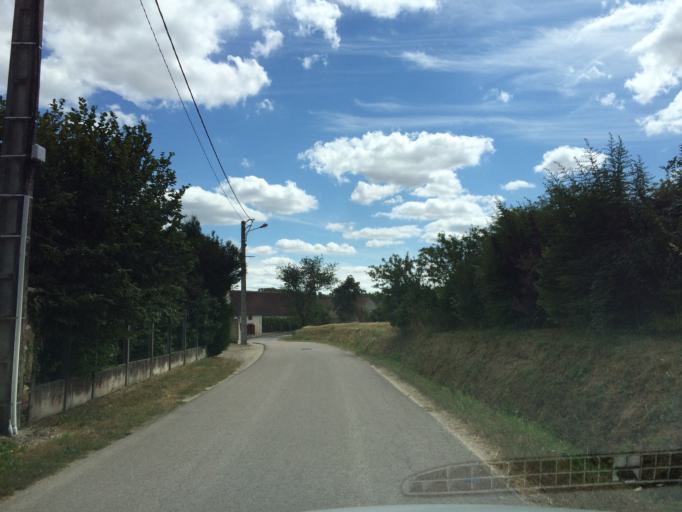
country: FR
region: Bourgogne
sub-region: Departement de l'Yonne
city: Fleury-la-Vallee
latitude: 47.8931
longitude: 3.4261
